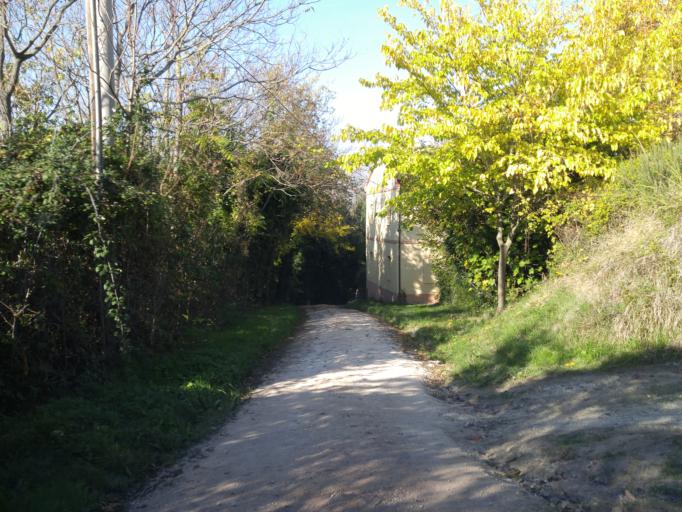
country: IT
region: The Marches
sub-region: Provincia di Pesaro e Urbino
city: Montemaggiore al Metauro
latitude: 43.7333
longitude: 12.9525
